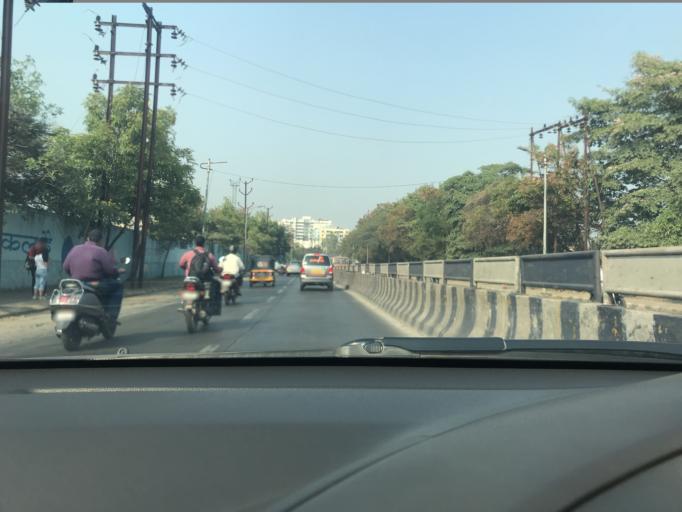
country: IN
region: Maharashtra
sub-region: Pune Division
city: Khadki
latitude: 18.5503
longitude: 73.8077
